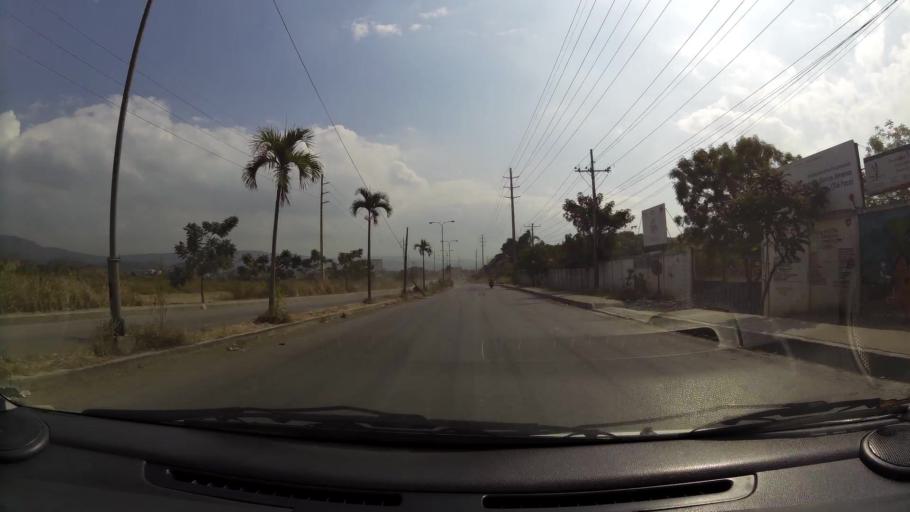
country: EC
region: Guayas
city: Santa Lucia
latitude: -2.1211
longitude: -79.9794
